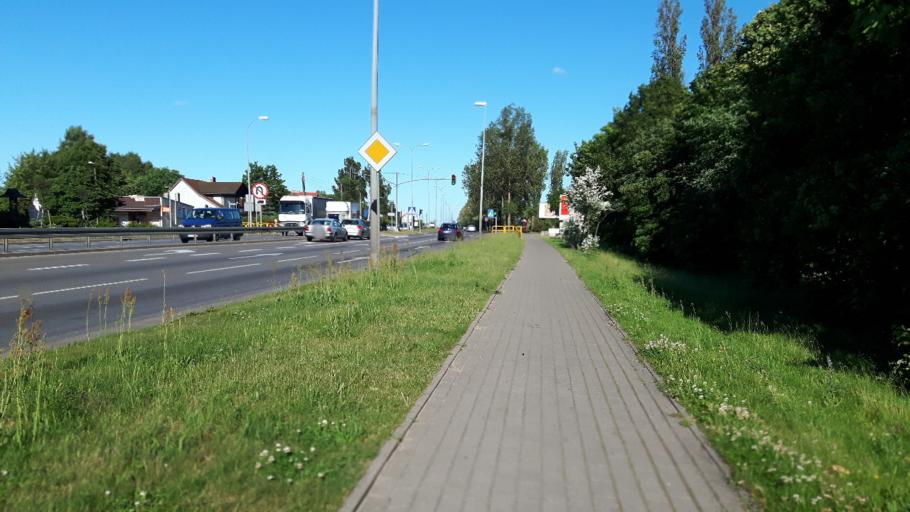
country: PL
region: Pomeranian Voivodeship
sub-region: Powiat wejherowski
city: Wejherowo
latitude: 54.6026
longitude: 18.2724
